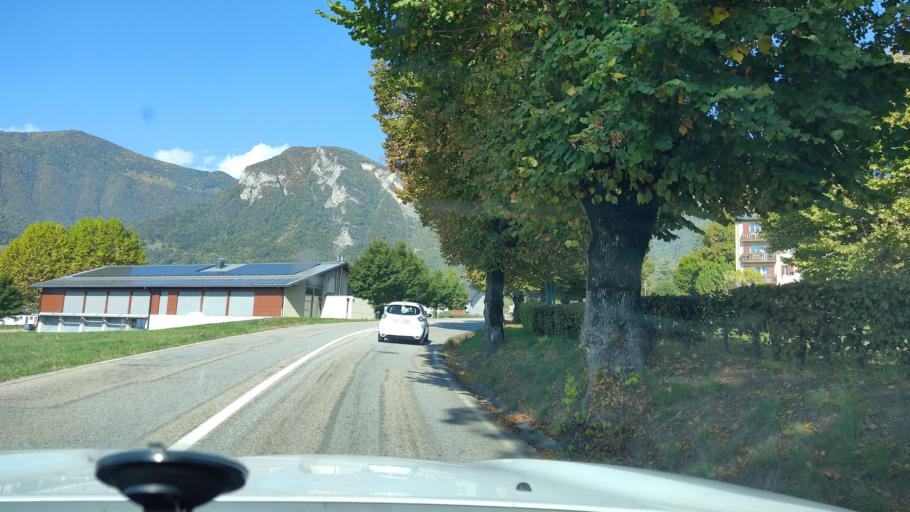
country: FR
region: Rhone-Alpes
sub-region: Departement de la Savoie
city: Coise-Saint-Jean-Pied-Gauthier
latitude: 45.5607
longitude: 6.1551
